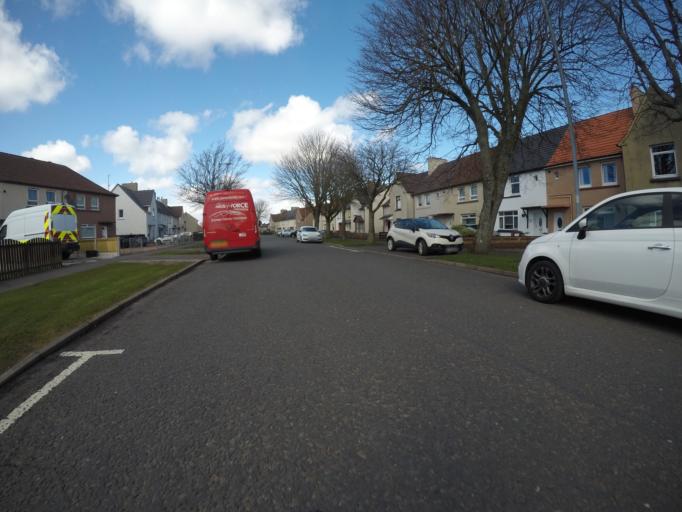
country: GB
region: Scotland
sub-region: North Ayrshire
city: Irvine
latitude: 55.6201
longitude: -4.6516
